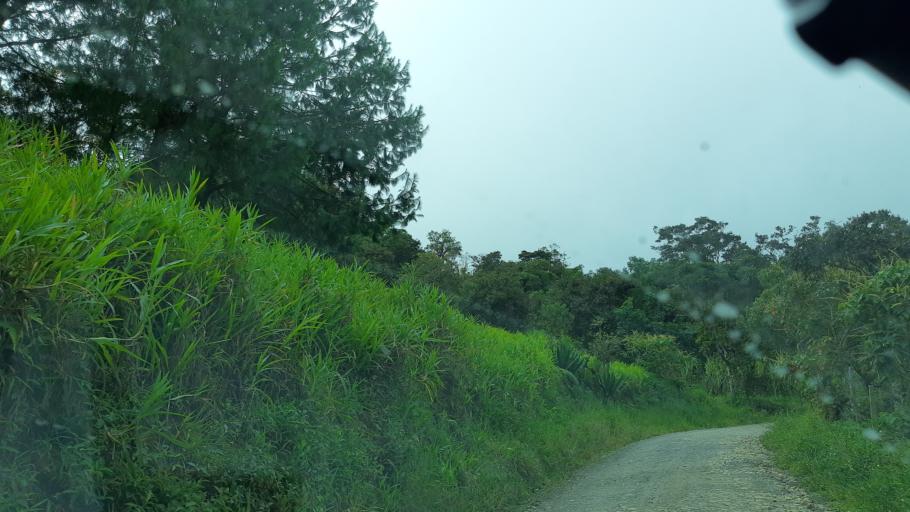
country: CO
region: Boyaca
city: Garagoa
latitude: 5.0454
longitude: -73.3477
